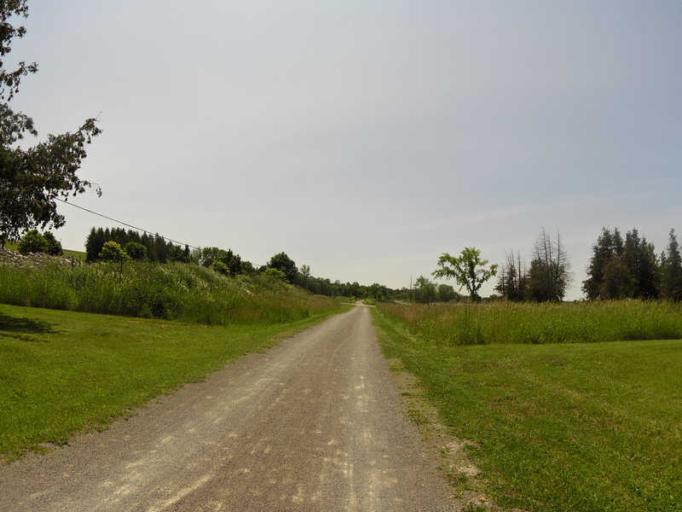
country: CA
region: Ontario
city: Peterborough
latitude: 44.4058
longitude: -78.2615
